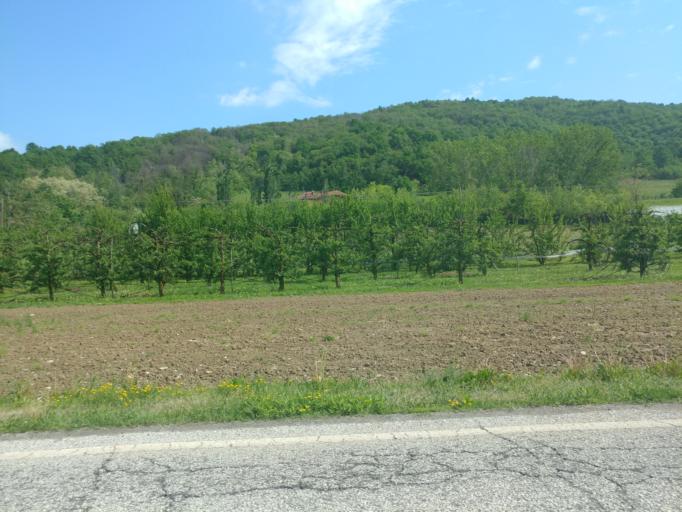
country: IT
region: Piedmont
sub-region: Provincia di Cuneo
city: Castellar
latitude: 44.6248
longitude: 7.4507
